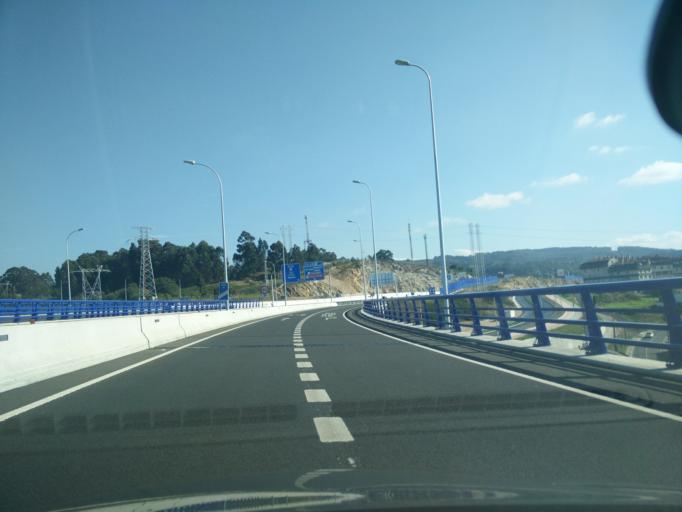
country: ES
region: Galicia
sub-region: Provincia da Coruna
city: A Coruna
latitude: 43.3359
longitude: -8.4219
